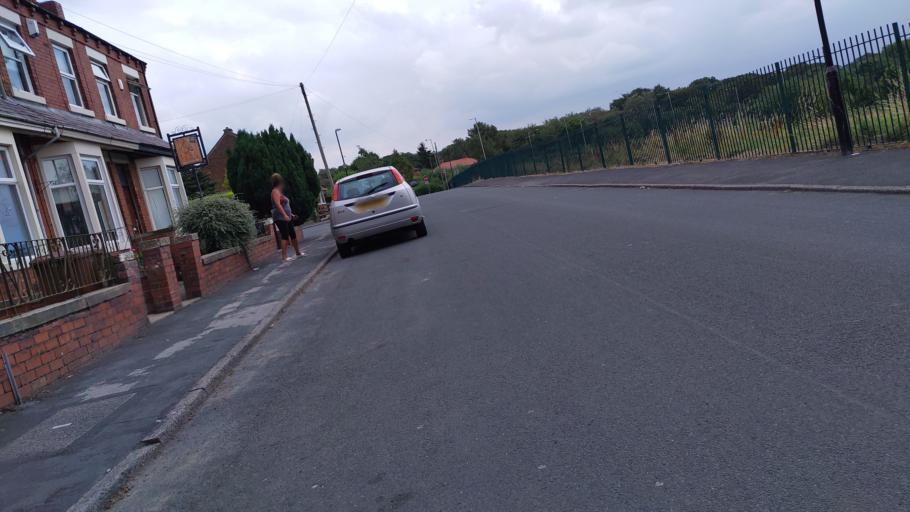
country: GB
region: England
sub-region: Lancashire
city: Coppull
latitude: 53.6400
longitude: -2.6494
